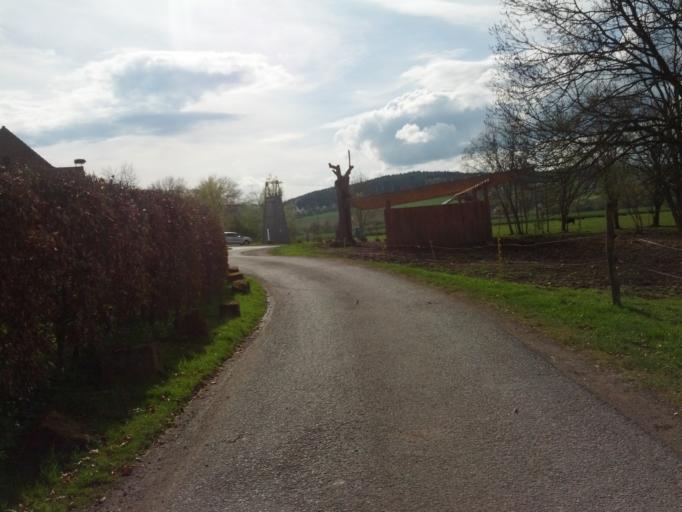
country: DE
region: Thuringia
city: Creuzburg
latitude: 51.0408
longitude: 10.2305
